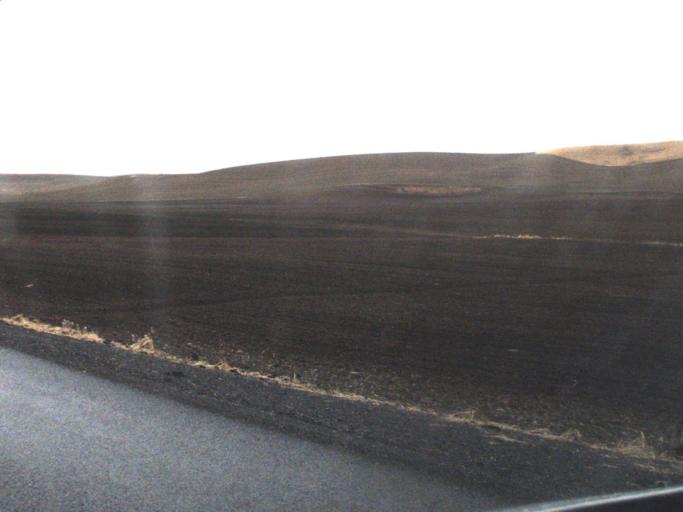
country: US
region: Washington
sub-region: Whitman County
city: Pullman
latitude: 46.7731
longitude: -117.2782
